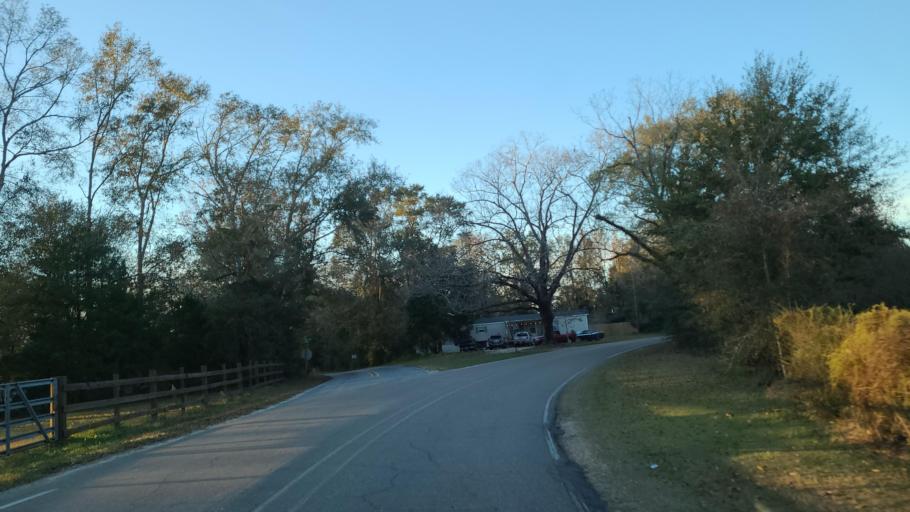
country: US
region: Mississippi
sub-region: Stone County
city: Wiggins
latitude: 30.9960
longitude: -89.2597
